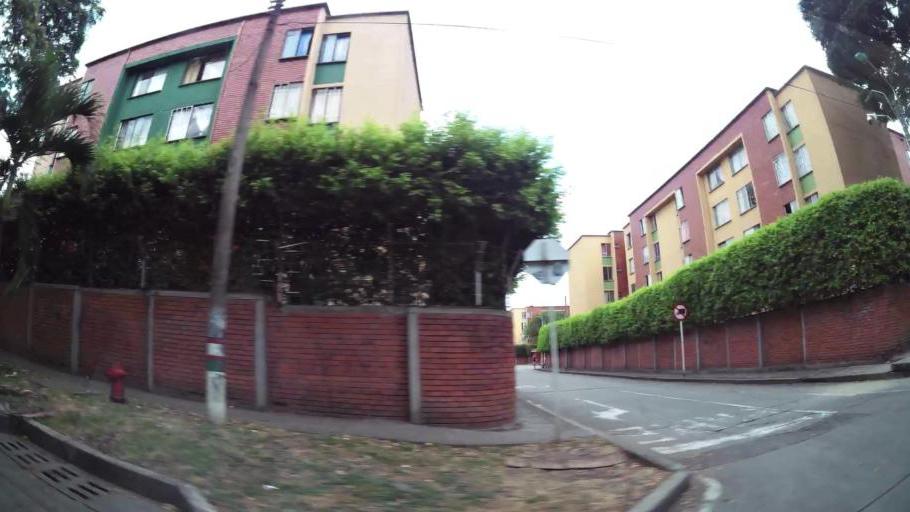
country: CO
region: Valle del Cauca
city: Cali
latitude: 3.4642
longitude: -76.5079
